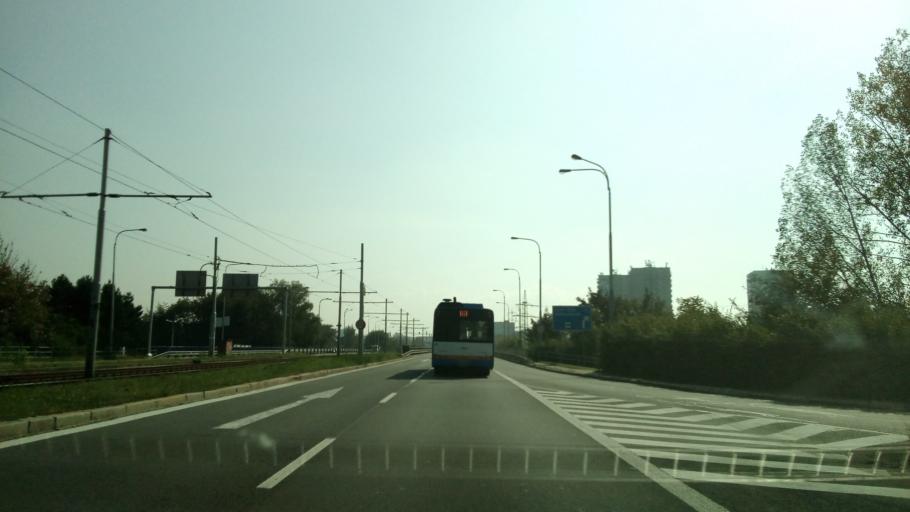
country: CZ
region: Moravskoslezsky
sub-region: Okres Ostrava-Mesto
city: Ostrava
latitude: 49.7994
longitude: 18.2472
